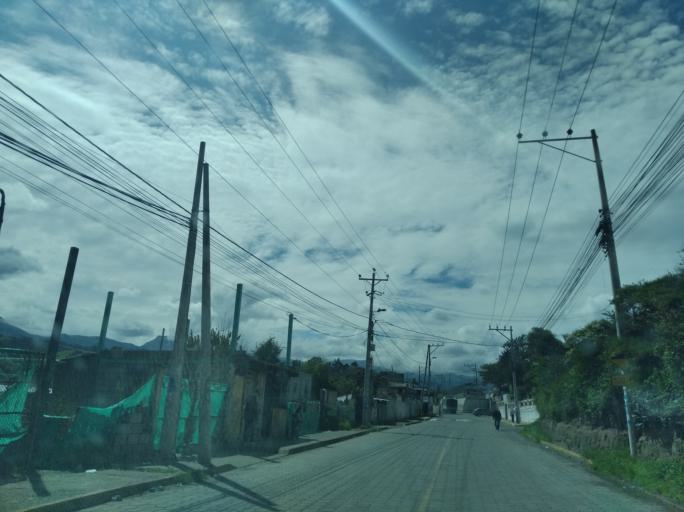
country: EC
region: Pichincha
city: Sangolqui
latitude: -0.2178
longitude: -78.3396
